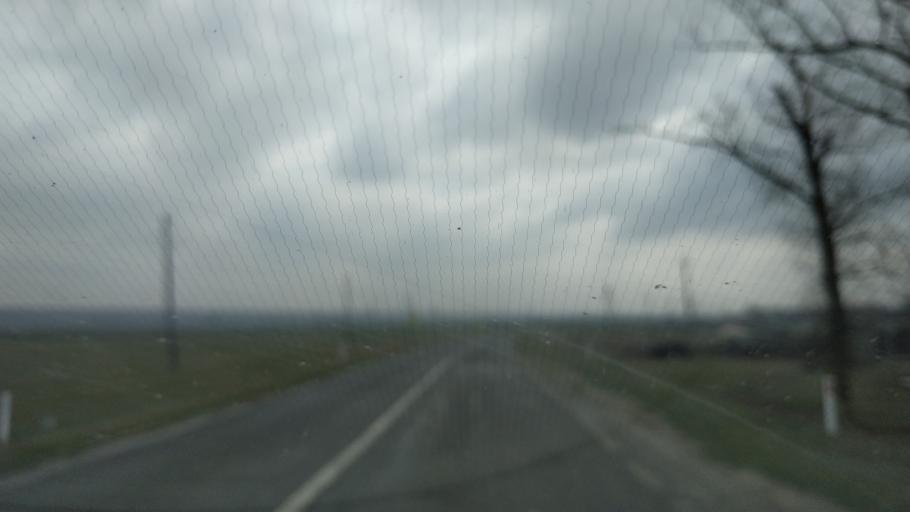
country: MD
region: Basarabeasca
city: Basarabeasca
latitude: 46.3989
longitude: 28.9045
